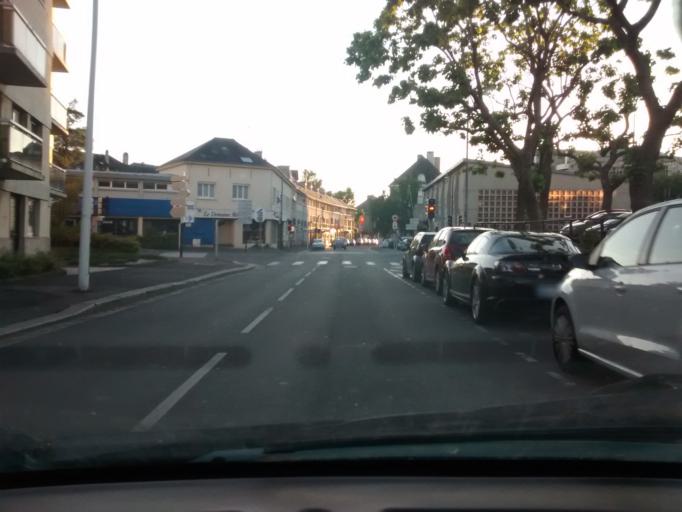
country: FR
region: Lower Normandy
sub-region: Departement de la Manche
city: Saint-Lo
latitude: 49.1135
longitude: -1.0897
